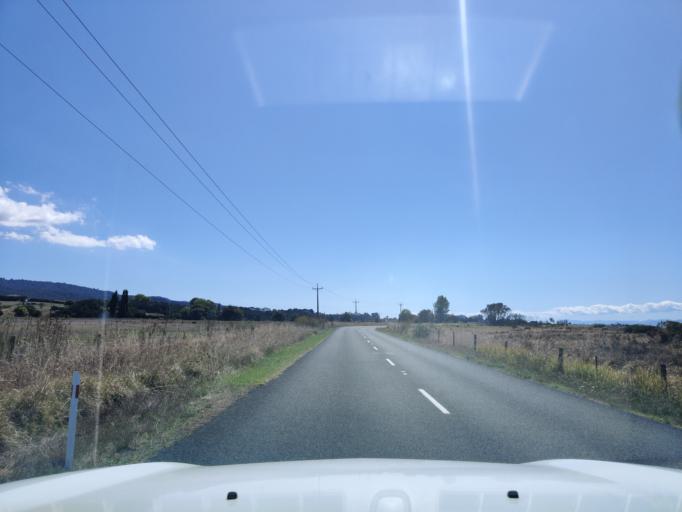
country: NZ
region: Waikato
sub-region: Thames-Coromandel District
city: Thames
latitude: -37.0703
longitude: 175.2958
